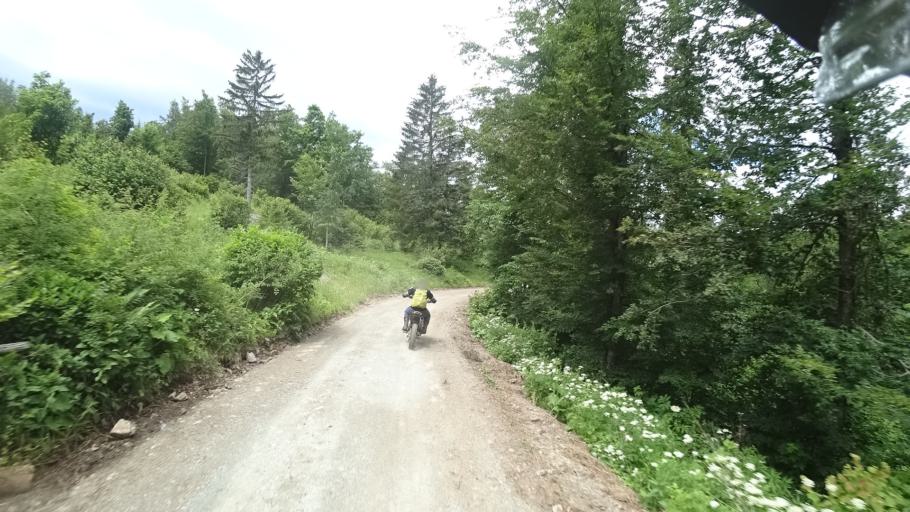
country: HR
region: Primorsko-Goranska
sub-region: Grad Delnice
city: Delnice
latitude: 45.3082
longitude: 14.7460
